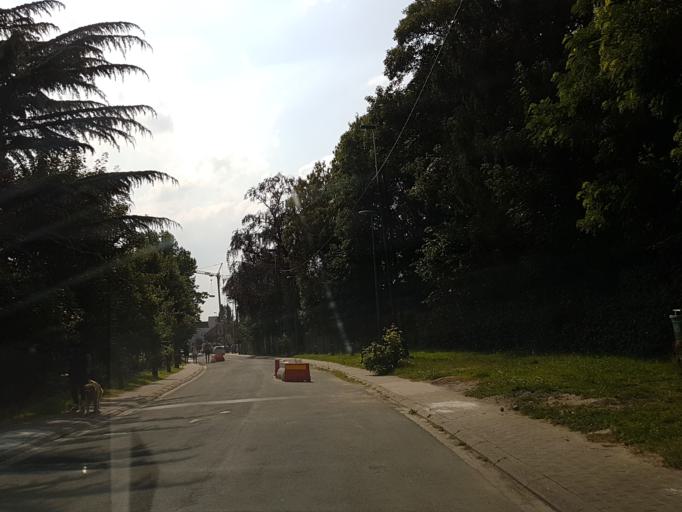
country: BE
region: Flanders
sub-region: Provincie Vlaams-Brabant
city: Kortenberg
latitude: 50.8876
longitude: 4.5489
